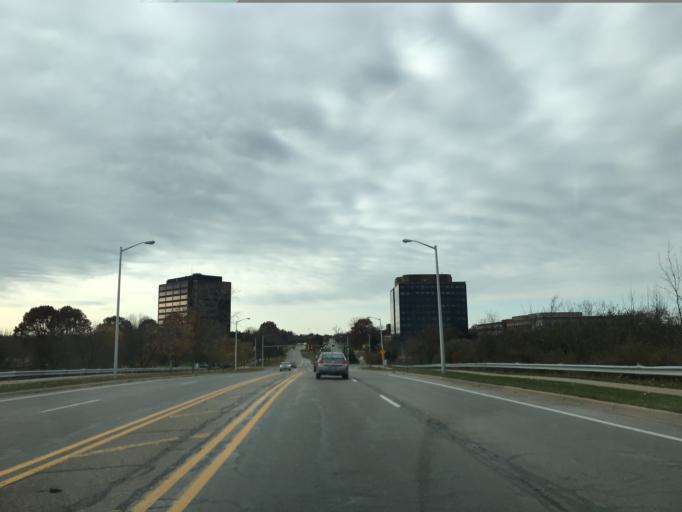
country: US
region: Michigan
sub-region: Washtenaw County
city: Ann Arbor
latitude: 42.2442
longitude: -83.7324
